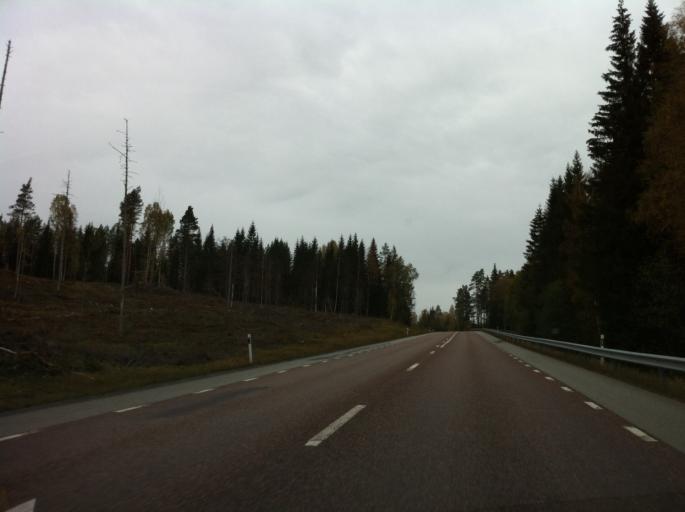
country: SE
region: Dalarna
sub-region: Ludvika Kommun
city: Grangesberg
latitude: 59.9938
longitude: 15.0157
